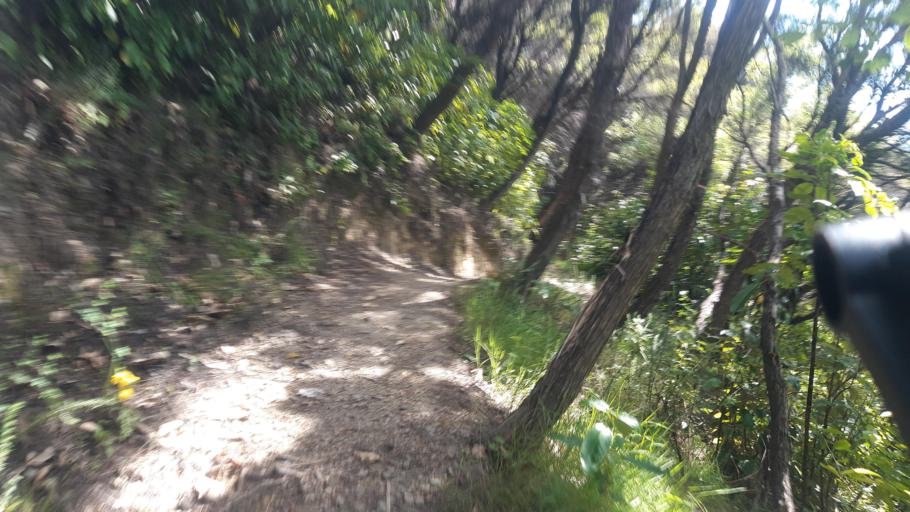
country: NZ
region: Marlborough
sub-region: Marlborough District
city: Picton
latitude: -41.2550
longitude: 174.0388
